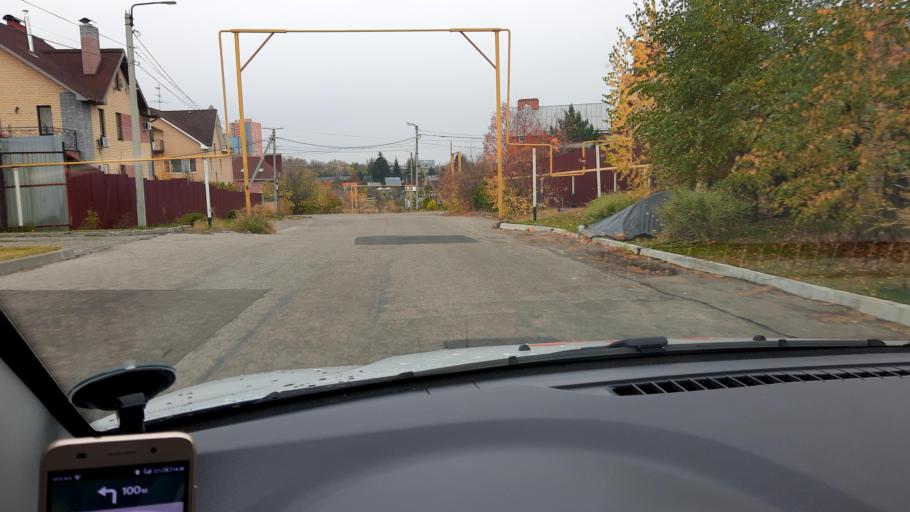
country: RU
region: Nizjnij Novgorod
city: Afonino
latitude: 56.2812
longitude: 44.0735
